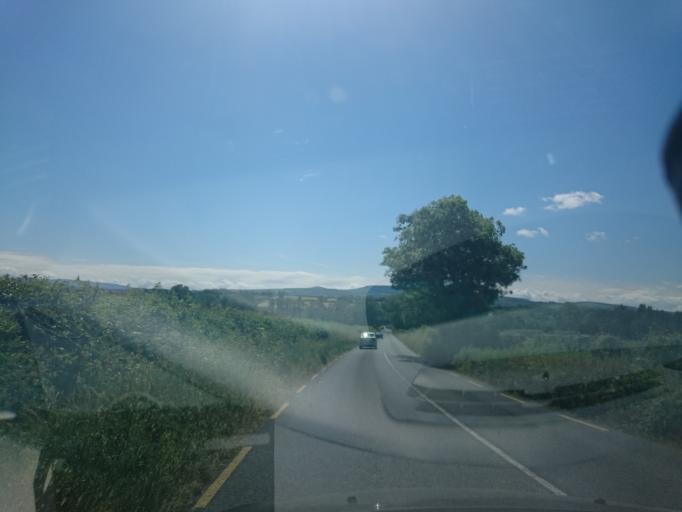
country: IE
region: Leinster
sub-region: County Carlow
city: Bagenalstown
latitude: 52.6307
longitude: -7.0490
